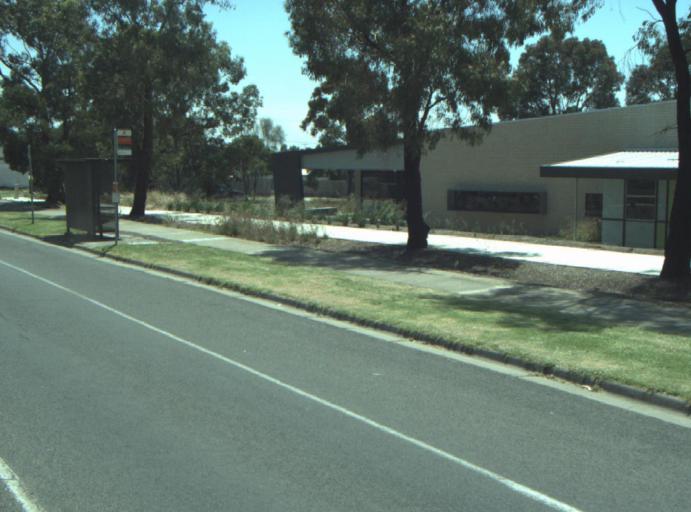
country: AU
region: Victoria
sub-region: Greater Geelong
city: Hamlyn Heights
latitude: -38.1226
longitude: 144.3279
